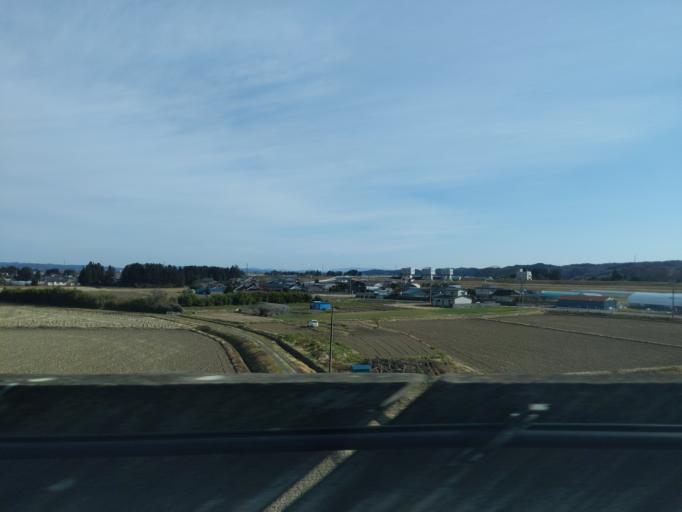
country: JP
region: Miyagi
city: Furukawa
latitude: 38.5294
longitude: 140.9607
